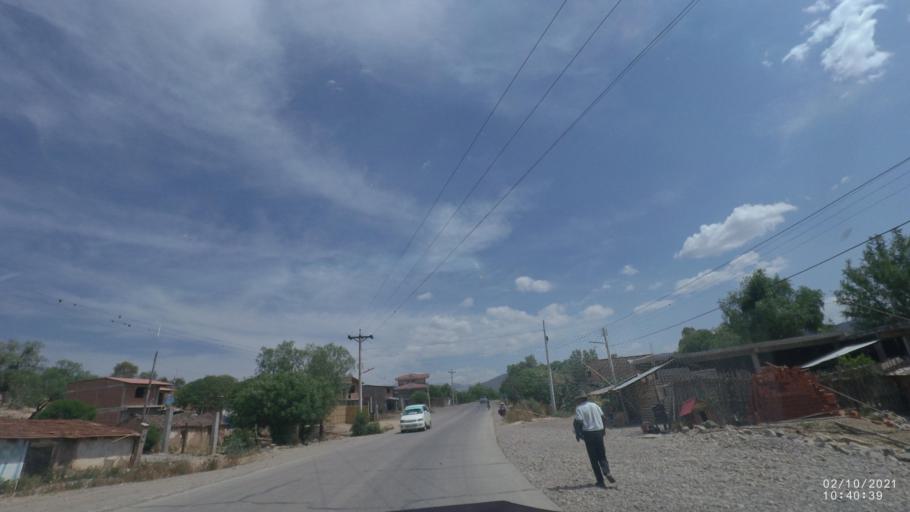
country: BO
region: Cochabamba
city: Capinota
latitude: -17.6196
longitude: -66.2877
